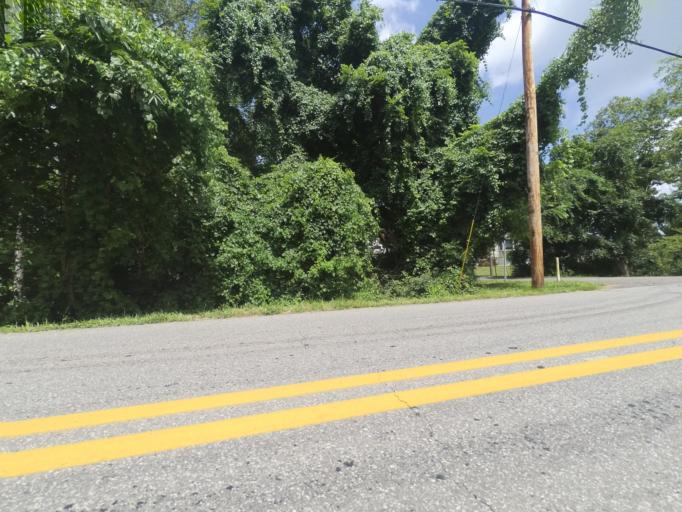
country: US
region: West Virginia
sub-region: Cabell County
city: Huntington
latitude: 38.4028
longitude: -82.3916
